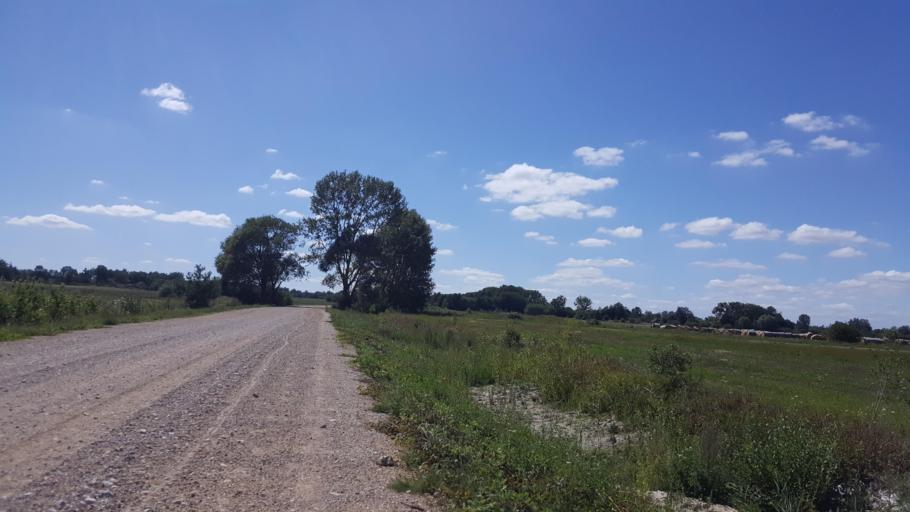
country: BY
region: Brest
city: Horad Kobryn
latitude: 52.3076
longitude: 24.3744
